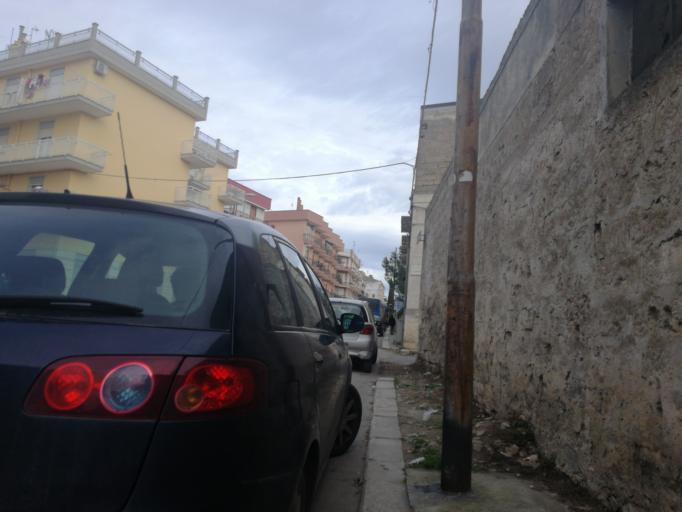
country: IT
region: Apulia
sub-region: Provincia di Bari
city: Ruvo di Puglia
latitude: 41.1188
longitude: 16.4788
